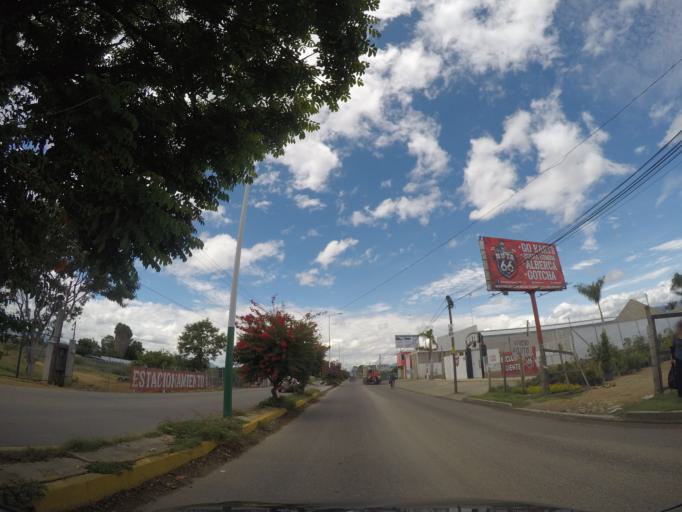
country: MX
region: Oaxaca
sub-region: Santa Cruz Xoxocotlan
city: San Isidro Monjas
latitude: 17.0072
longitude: -96.7371
